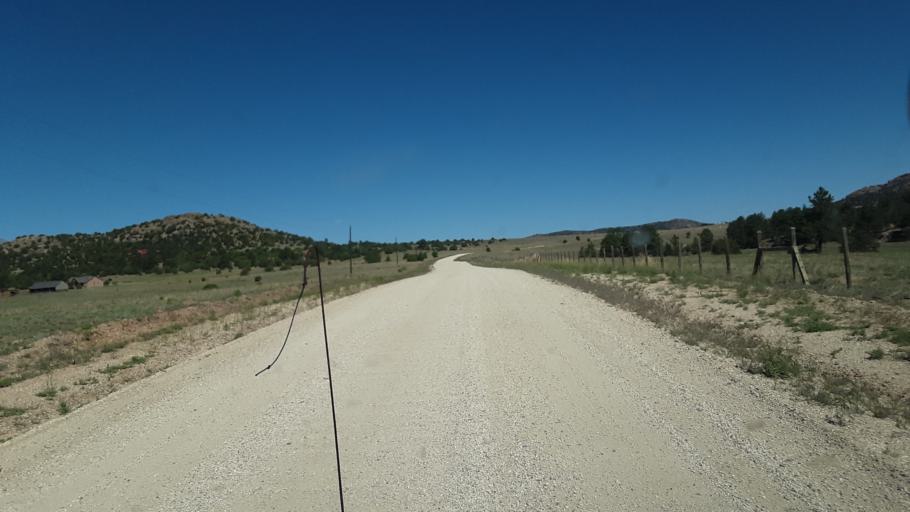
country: US
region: Colorado
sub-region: Custer County
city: Westcliffe
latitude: 38.2182
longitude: -105.4521
